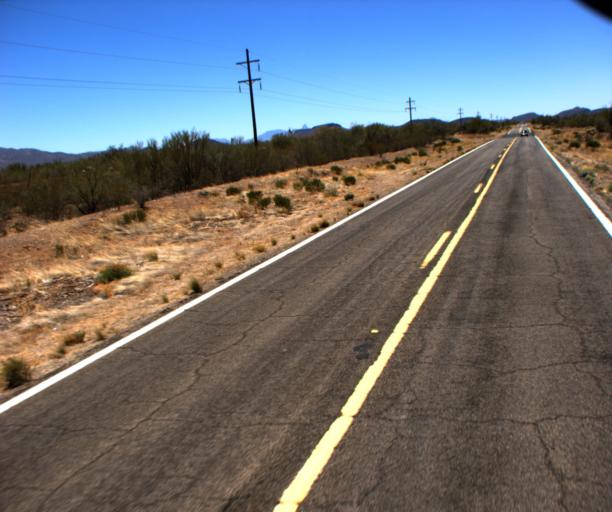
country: US
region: Arizona
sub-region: Pima County
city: Sells
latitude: 32.0275
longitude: -112.0073
